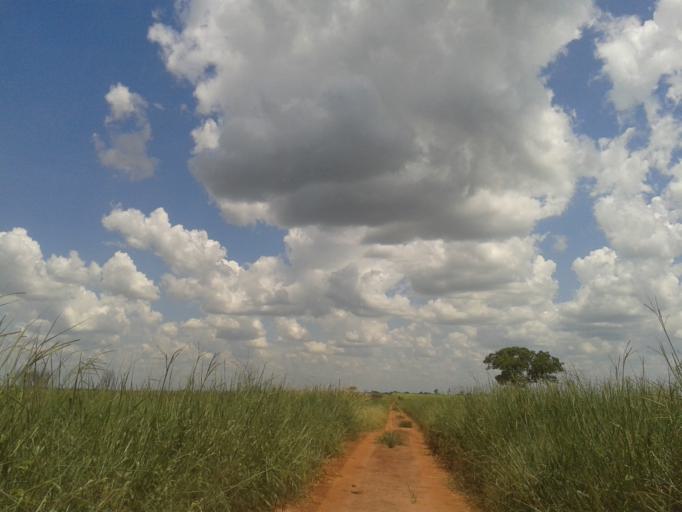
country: BR
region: Minas Gerais
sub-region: Santa Vitoria
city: Santa Vitoria
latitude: -19.1720
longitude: -50.4548
